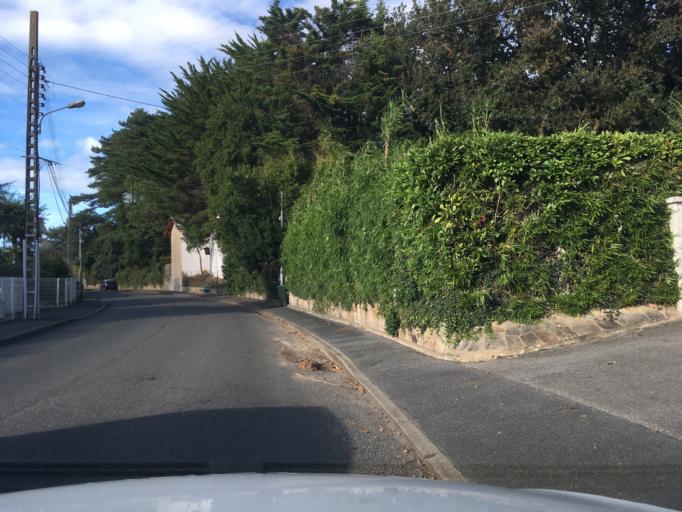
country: FR
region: Aquitaine
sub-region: Departement des Pyrenees-Atlantiques
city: Biarritz
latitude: 43.4644
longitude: -1.5552
